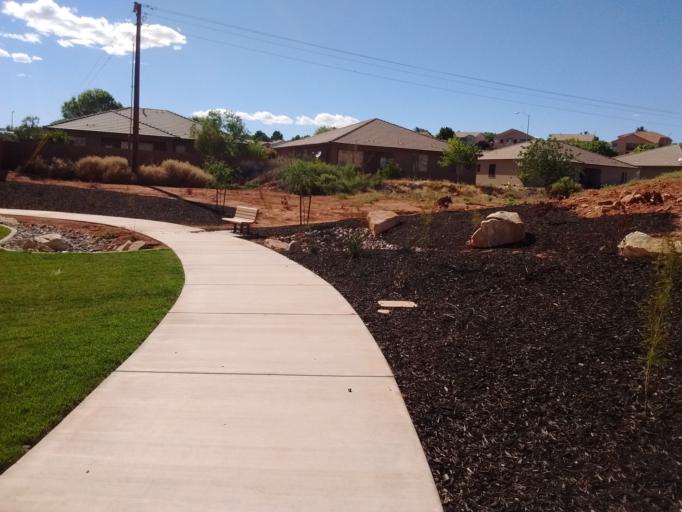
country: US
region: Utah
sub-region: Washington County
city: Washington
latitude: 37.1118
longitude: -113.5222
